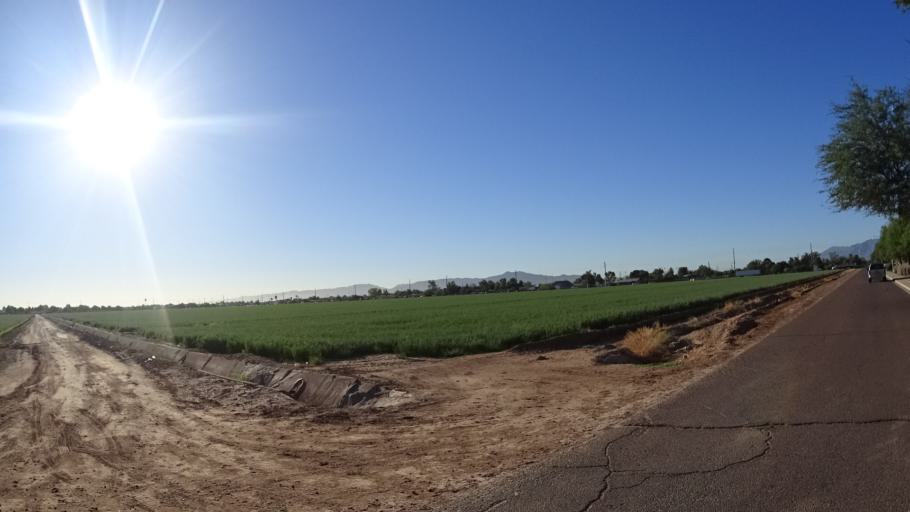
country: US
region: Arizona
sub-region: Maricopa County
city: Tolleson
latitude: 33.4260
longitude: -112.2126
